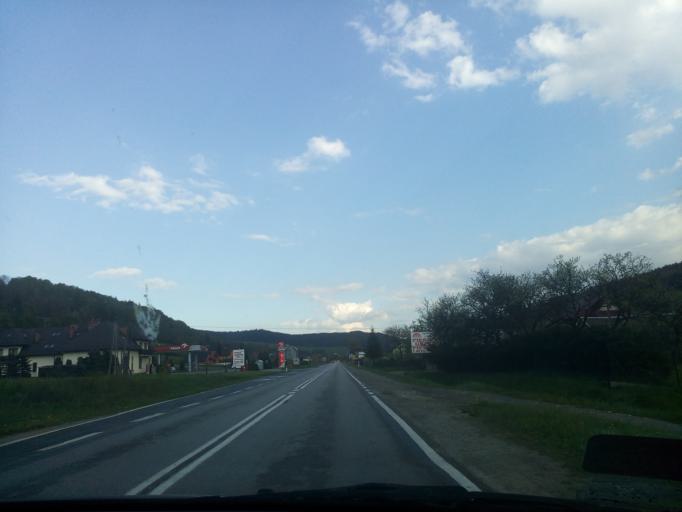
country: PL
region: Lesser Poland Voivodeship
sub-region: Powiat nowosadecki
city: Labowa
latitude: 49.5065
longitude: 20.8925
